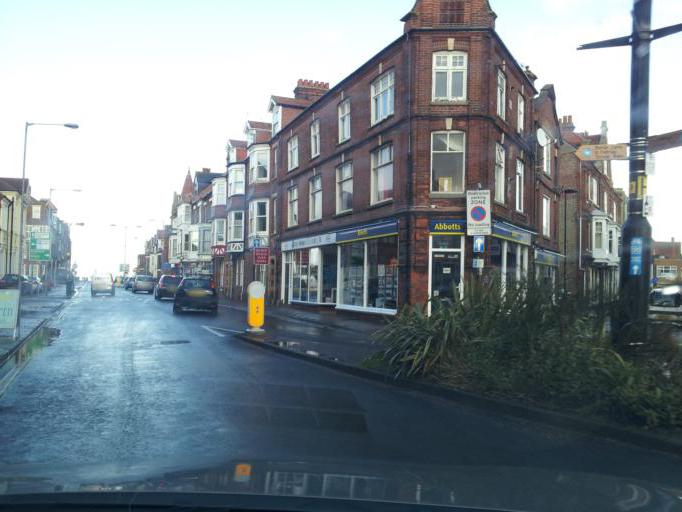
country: GB
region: England
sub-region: Norfolk
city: Cromer
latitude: 52.9308
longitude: 1.2977
